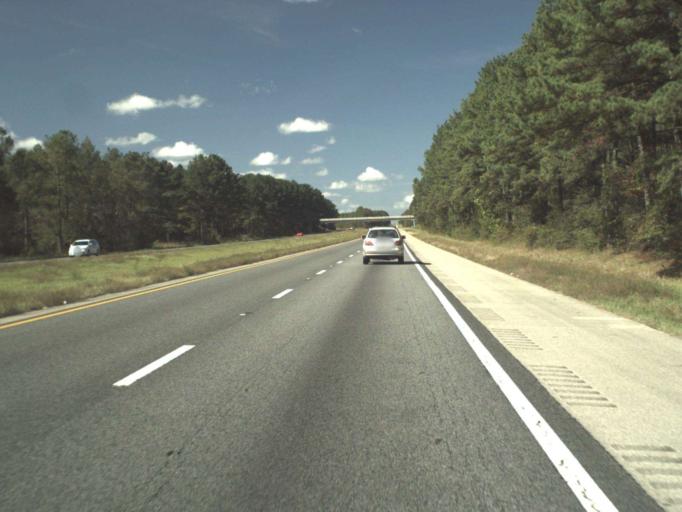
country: US
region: Florida
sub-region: Washington County
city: Chipley
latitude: 30.7453
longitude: -85.4555
